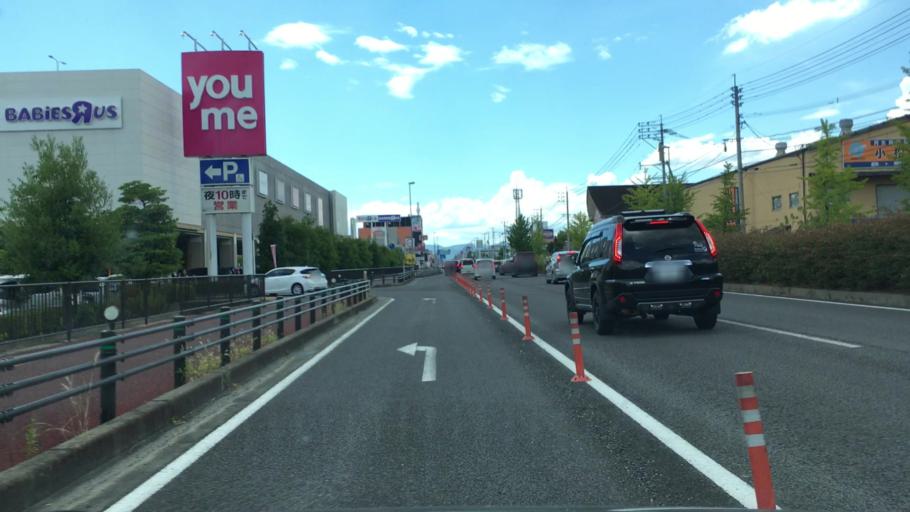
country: JP
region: Saga Prefecture
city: Saga-shi
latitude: 33.2768
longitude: 130.3078
